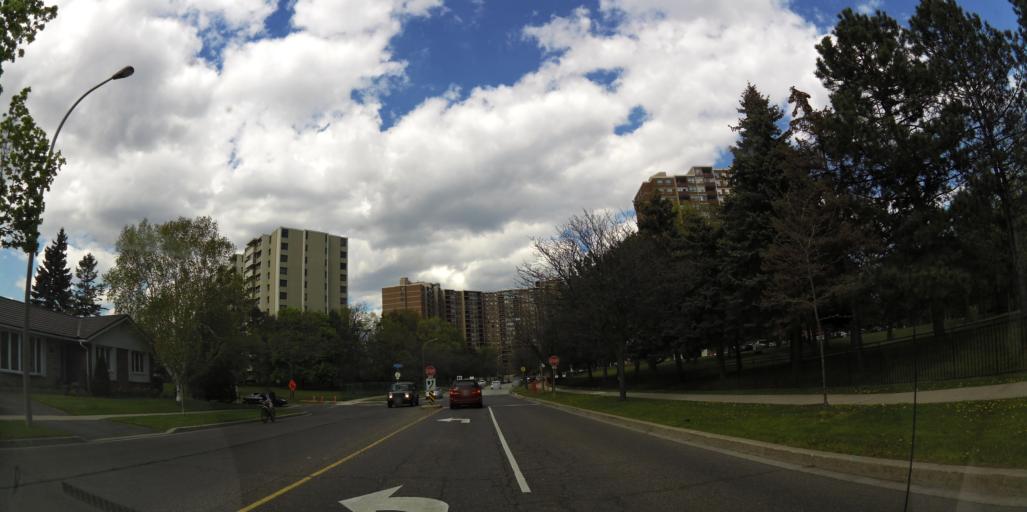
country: CA
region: Ontario
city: Etobicoke
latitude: 43.6548
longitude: -79.5727
